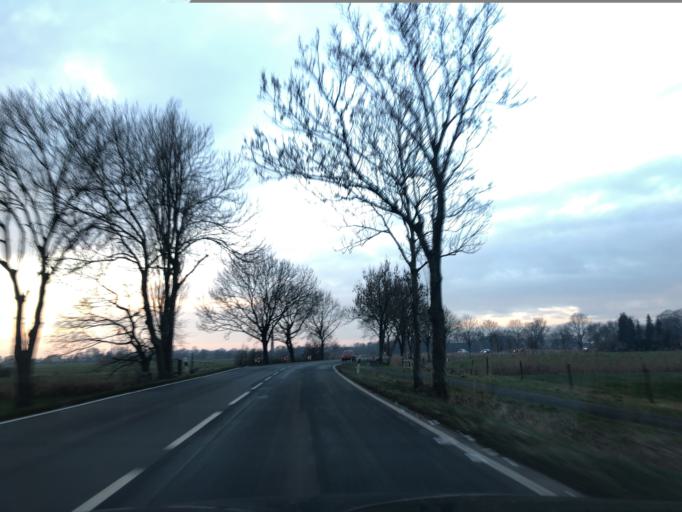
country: DE
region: Lower Saxony
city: Lemwerder
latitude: 53.1371
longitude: 8.5982
